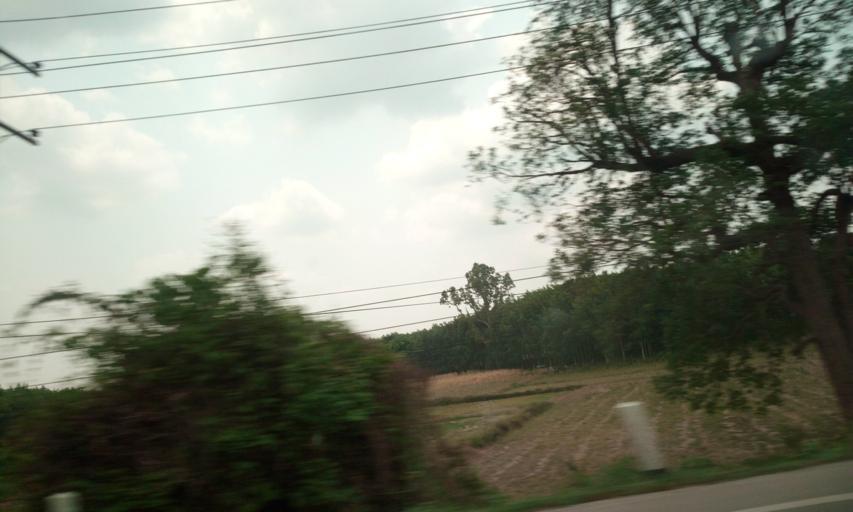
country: TH
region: Chiang Rai
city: Thoeng
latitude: 19.6752
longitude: 100.2265
